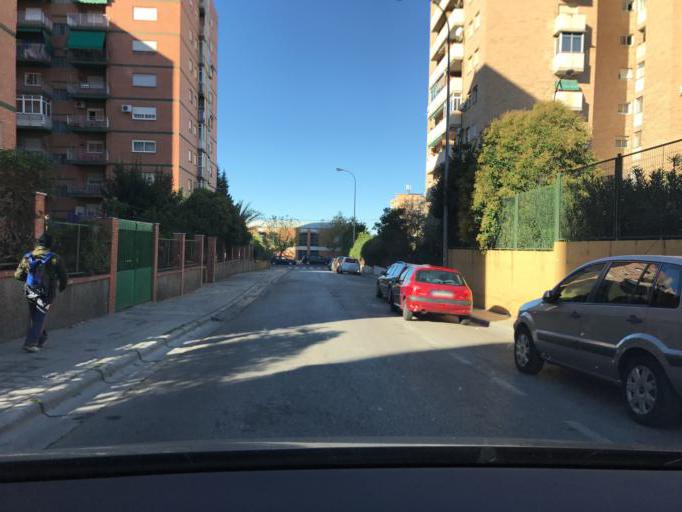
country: ES
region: Andalusia
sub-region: Provincia de Granada
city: Granada
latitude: 37.2037
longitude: -3.5992
